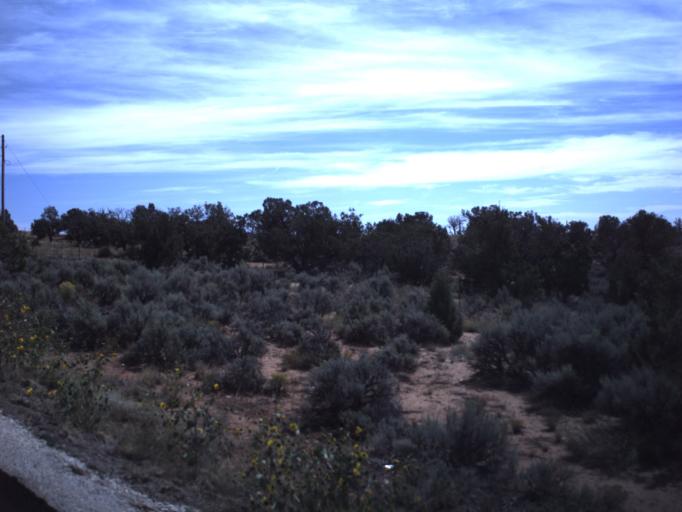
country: US
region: Utah
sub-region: San Juan County
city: Blanding
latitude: 37.5736
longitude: -109.4952
